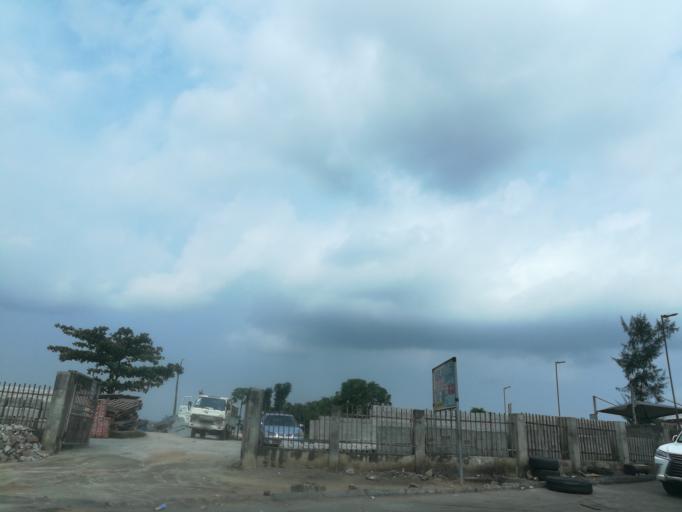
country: NG
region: Lagos
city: Ikeja
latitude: 6.6237
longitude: 3.3641
